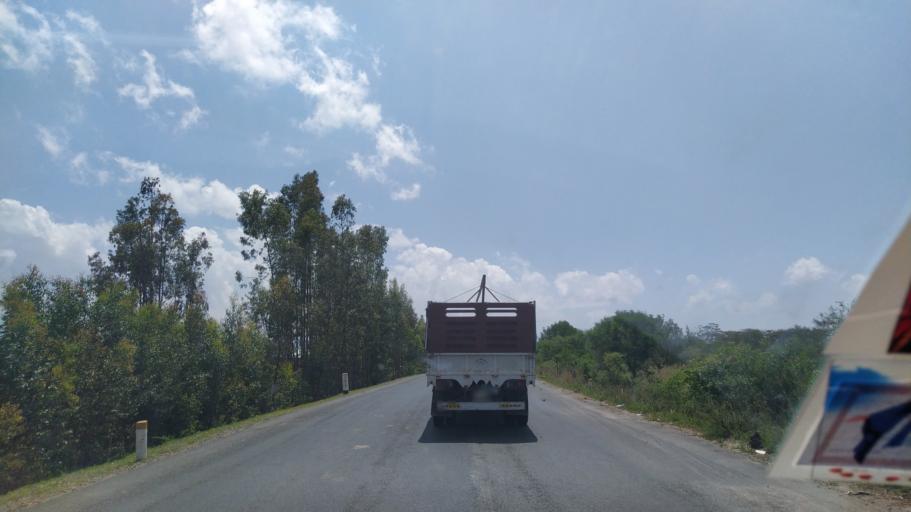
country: ET
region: Southern Nations, Nationalities, and People's Region
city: Butajira
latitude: 7.7802
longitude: 38.1384
